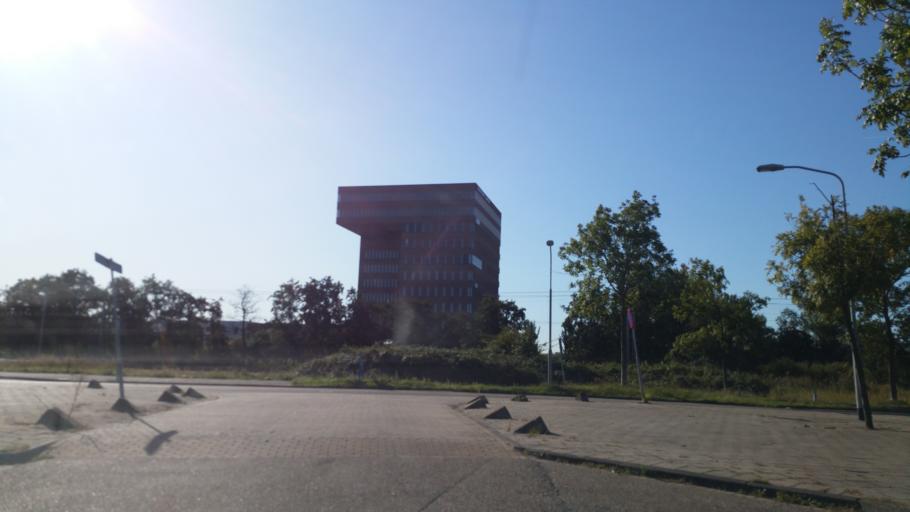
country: NL
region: North Holland
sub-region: Gemeente Haarlem
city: Haarlem
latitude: 52.3833
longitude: 4.6679
